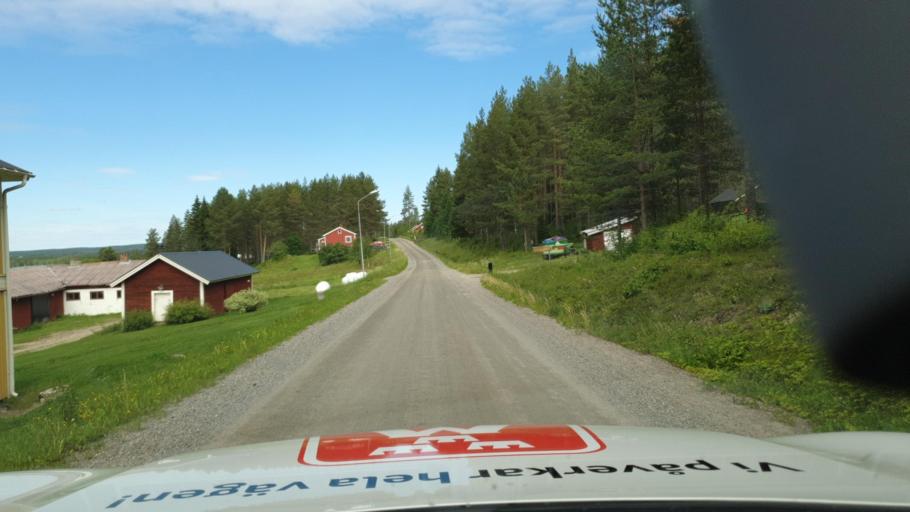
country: SE
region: Vaesterbotten
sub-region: Skelleftea Kommun
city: Forsbacka
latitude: 64.6657
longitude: 20.5339
